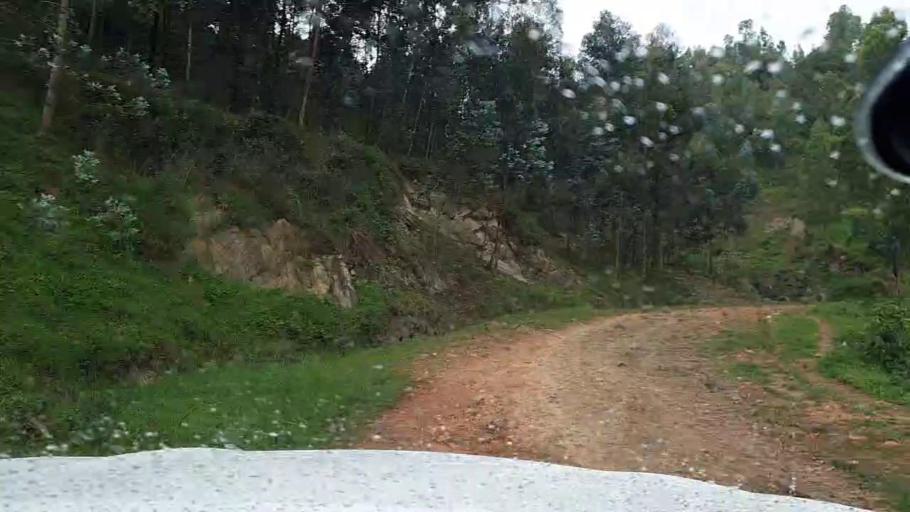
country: RW
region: Western Province
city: Kibuye
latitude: -2.0769
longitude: 29.4442
